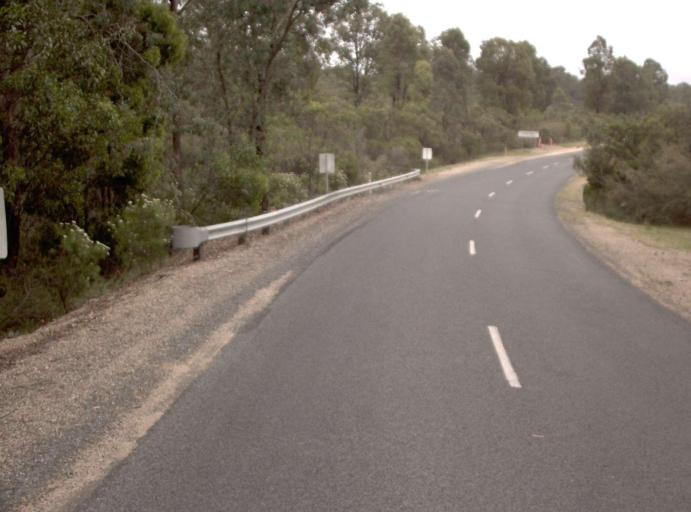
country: AU
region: Victoria
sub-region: Wellington
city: Heyfield
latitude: -37.9297
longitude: 146.7553
